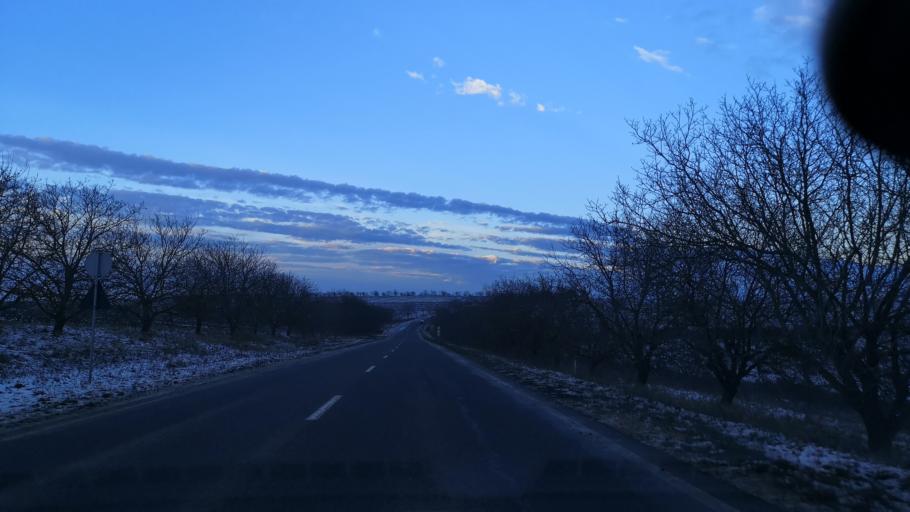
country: MD
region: Orhei
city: Orhei
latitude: 47.5693
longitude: 28.7972
